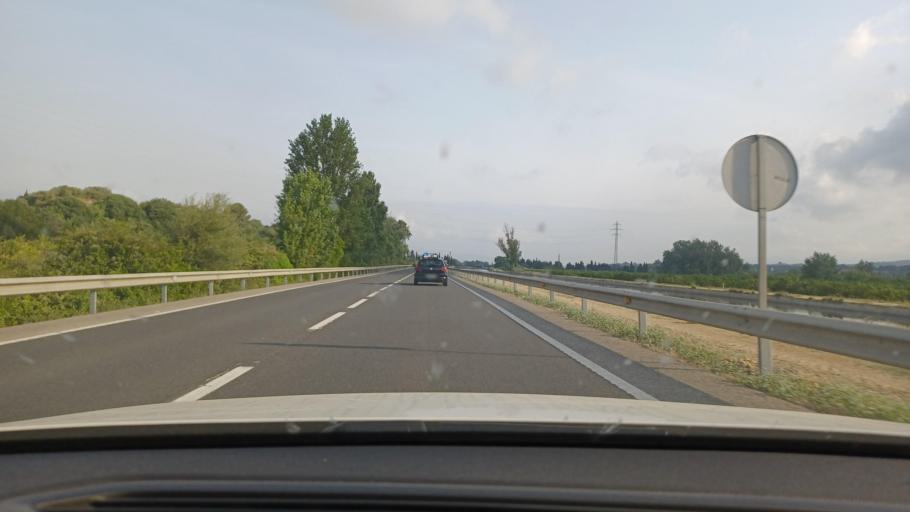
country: ES
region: Catalonia
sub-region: Provincia de Tarragona
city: Masdenverge
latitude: 40.7610
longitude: 0.5345
